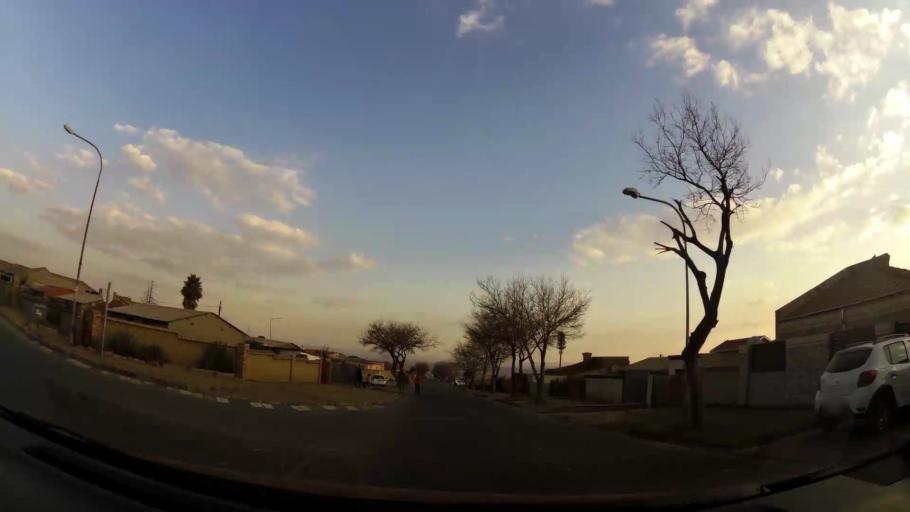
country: ZA
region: Gauteng
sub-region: City of Johannesburg Metropolitan Municipality
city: Soweto
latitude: -26.2196
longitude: 27.8922
